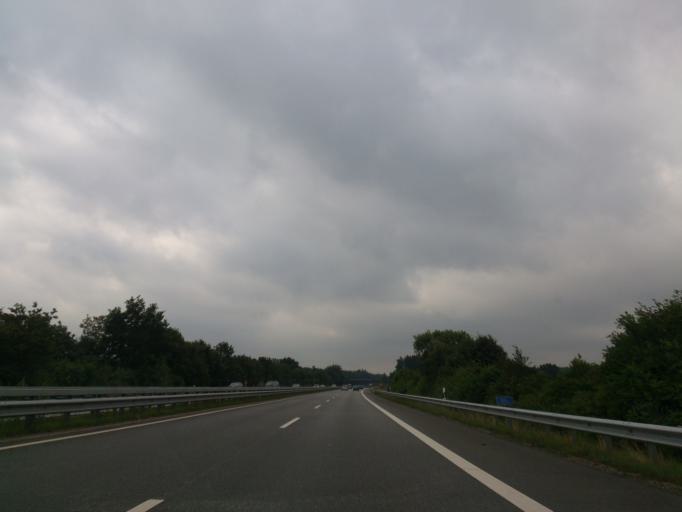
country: DE
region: Schleswig-Holstein
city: Kaaks
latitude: 53.9930
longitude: 9.4875
